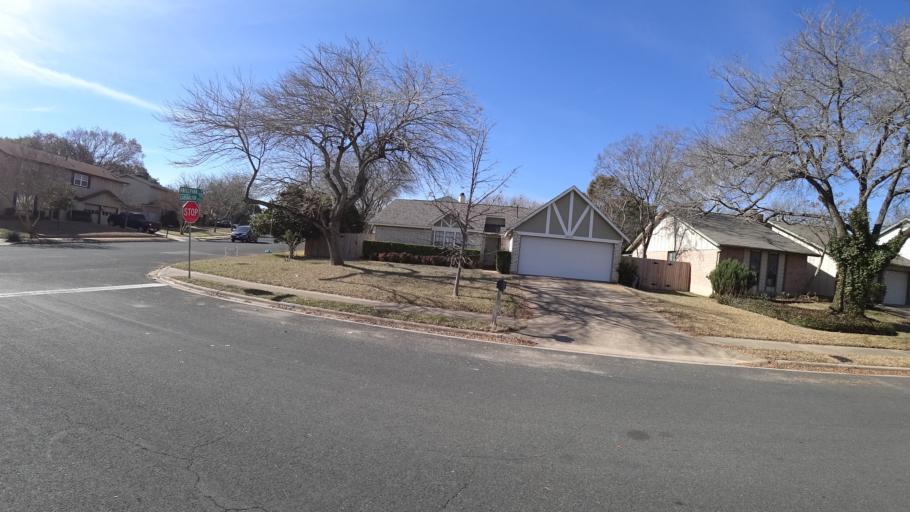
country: US
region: Texas
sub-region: Travis County
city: Wells Branch
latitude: 30.3904
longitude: -97.6913
